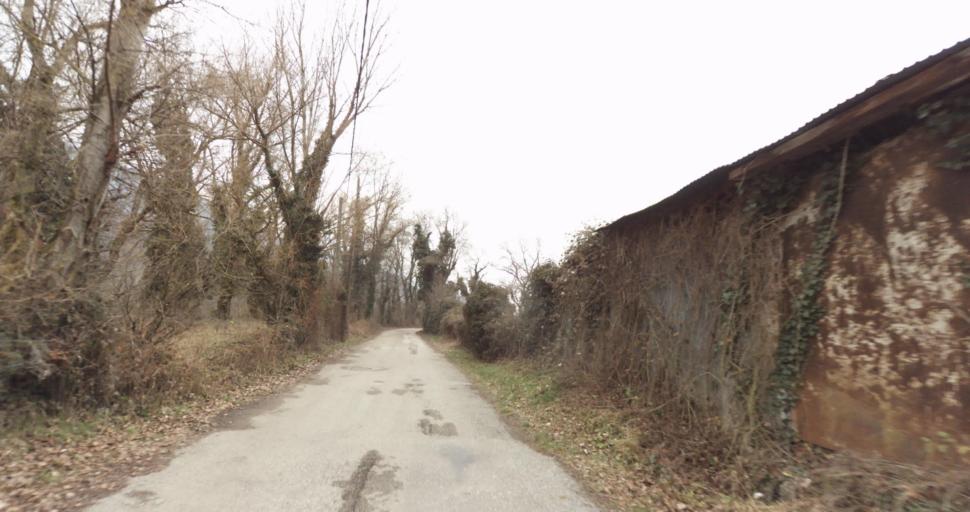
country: FR
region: Rhone-Alpes
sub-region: Departement de l'Isere
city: Vif
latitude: 45.0405
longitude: 5.6569
